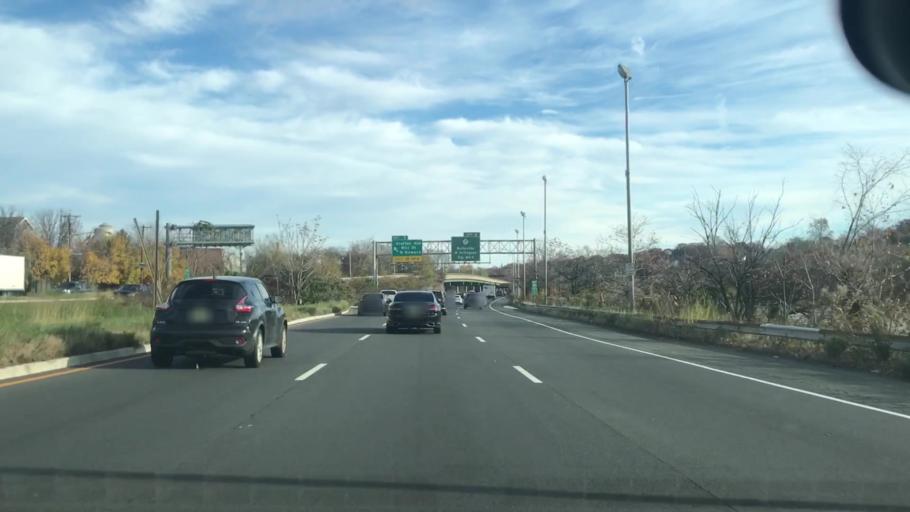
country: US
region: New Jersey
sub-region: Hudson County
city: Kearny
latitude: 40.7740
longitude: -74.1545
